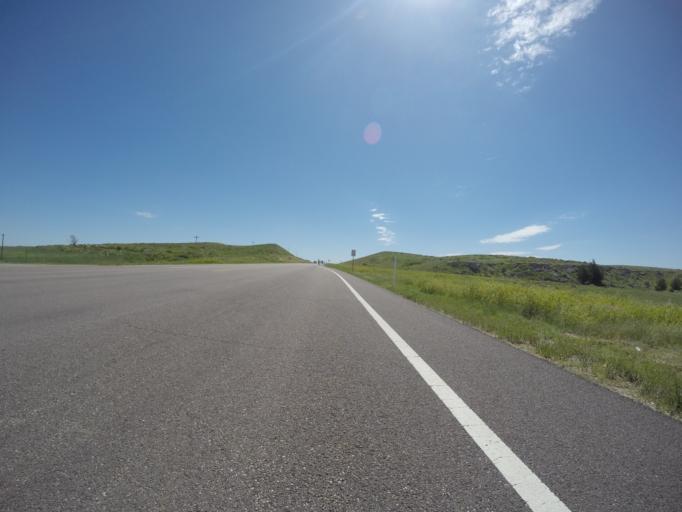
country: US
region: Kansas
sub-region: Rawlins County
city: Atwood
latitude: 39.8134
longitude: -100.9997
